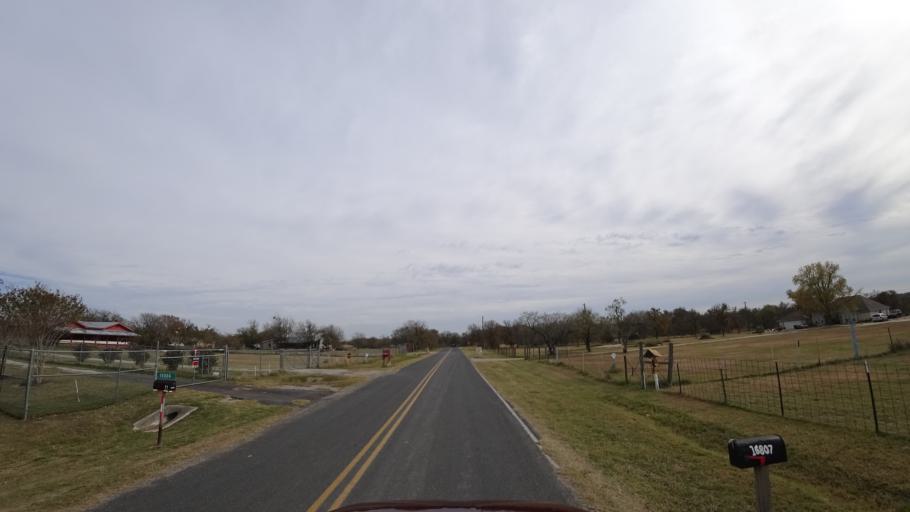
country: US
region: Texas
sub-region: Travis County
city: Garfield
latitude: 30.1383
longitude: -97.5770
